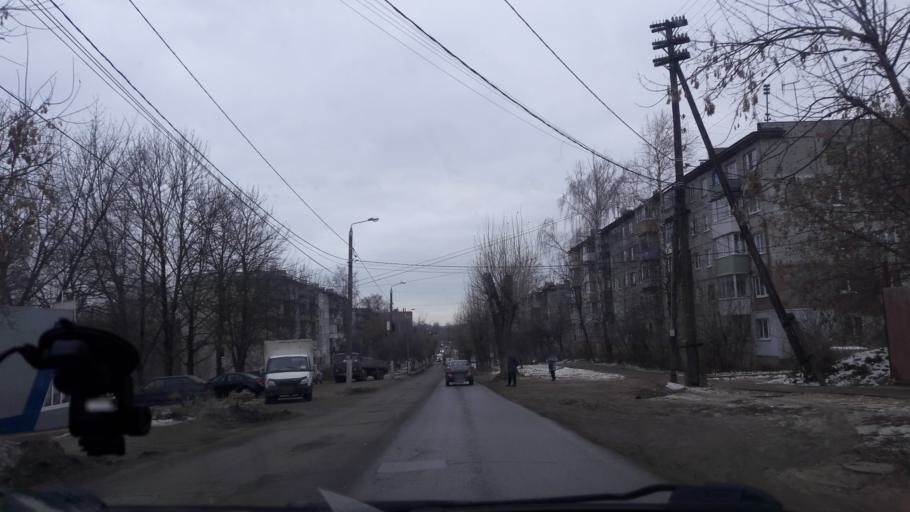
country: RU
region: Tula
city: Tula
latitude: 54.2030
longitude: 37.6585
